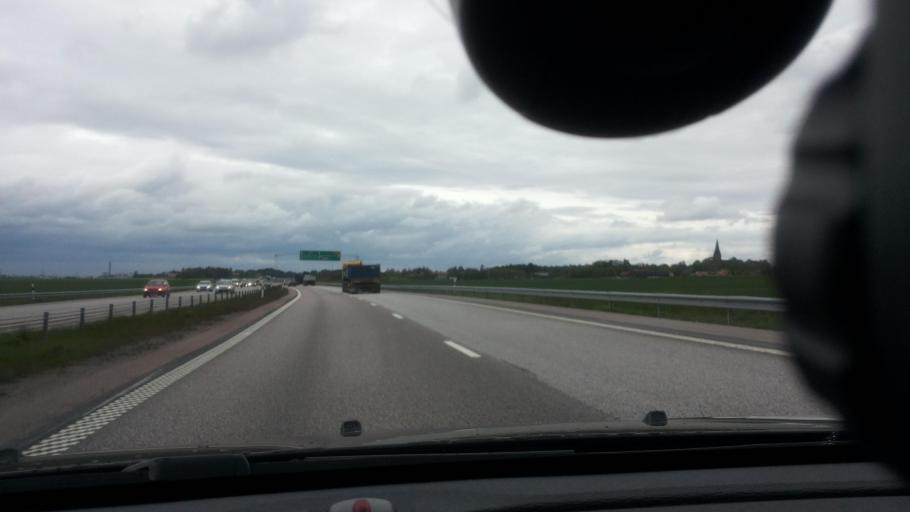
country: SE
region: Uppsala
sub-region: Uppsala Kommun
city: Saevja
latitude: 59.8226
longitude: 17.7491
